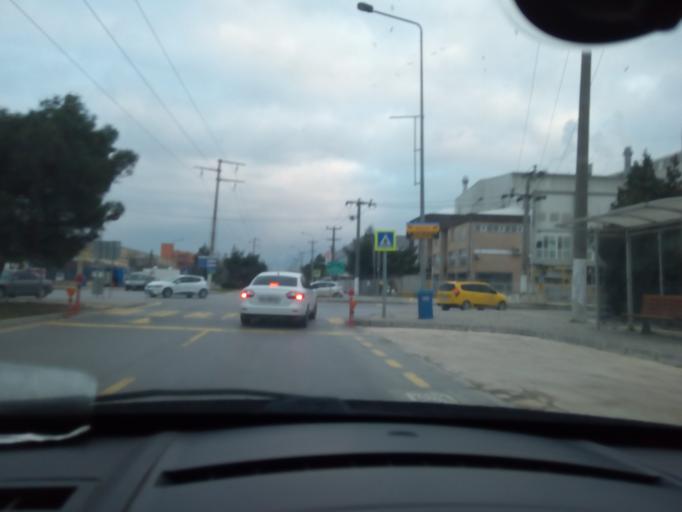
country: TR
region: Bursa
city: Niluefer
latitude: 40.2430
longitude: 28.9616
